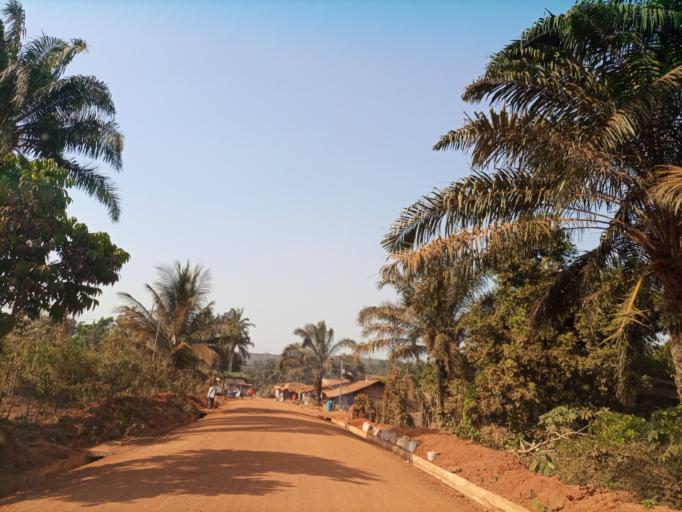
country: NG
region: Enugu
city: Aku
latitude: 6.7015
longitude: 7.3260
